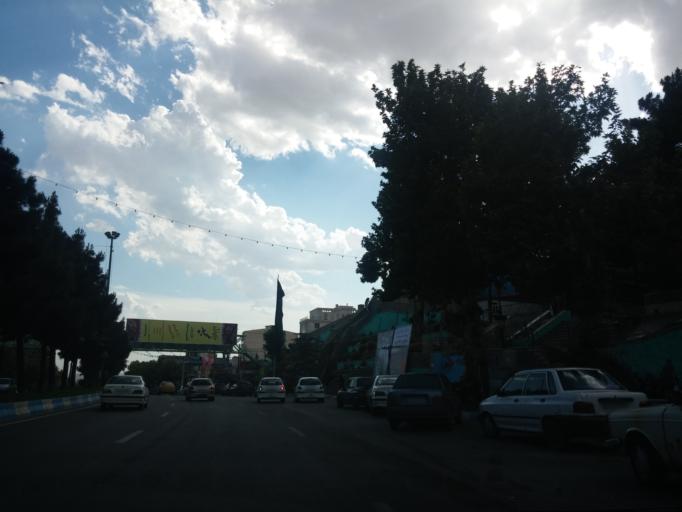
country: IR
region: Tehran
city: Damavand
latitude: 35.7355
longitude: 51.9093
